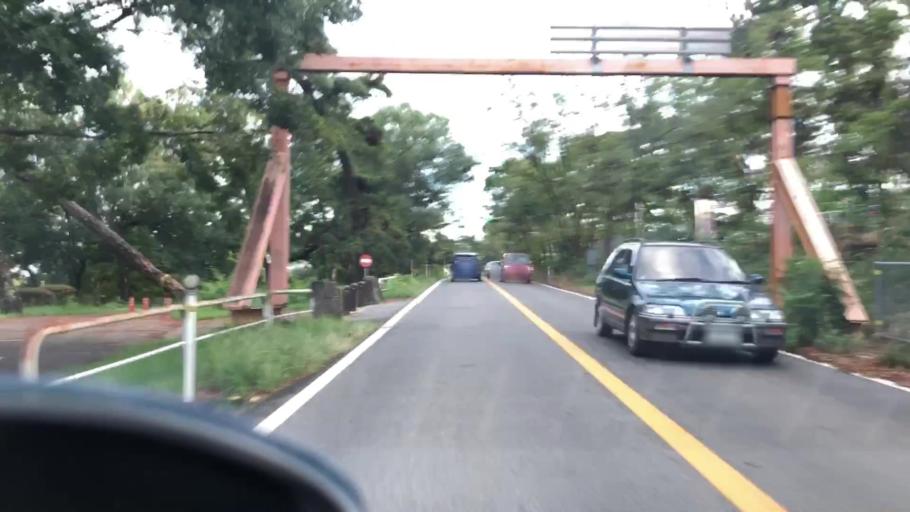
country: JP
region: Hyogo
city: Itami
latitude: 34.7640
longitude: 135.3723
